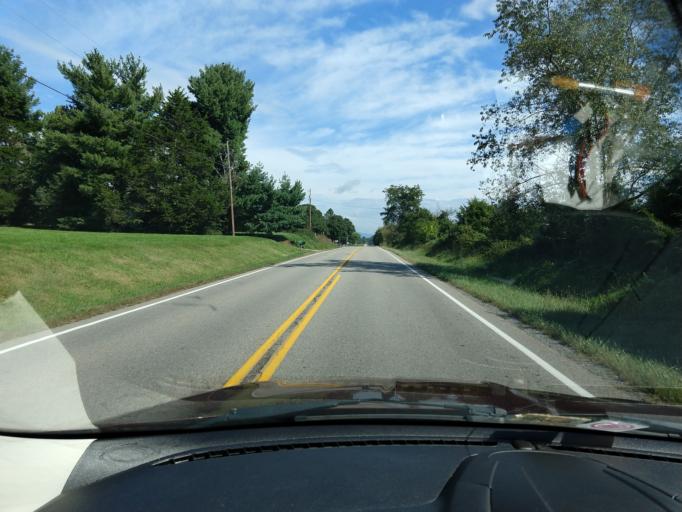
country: US
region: Virginia
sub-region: Augusta County
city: Crimora
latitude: 38.1895
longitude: -78.8401
